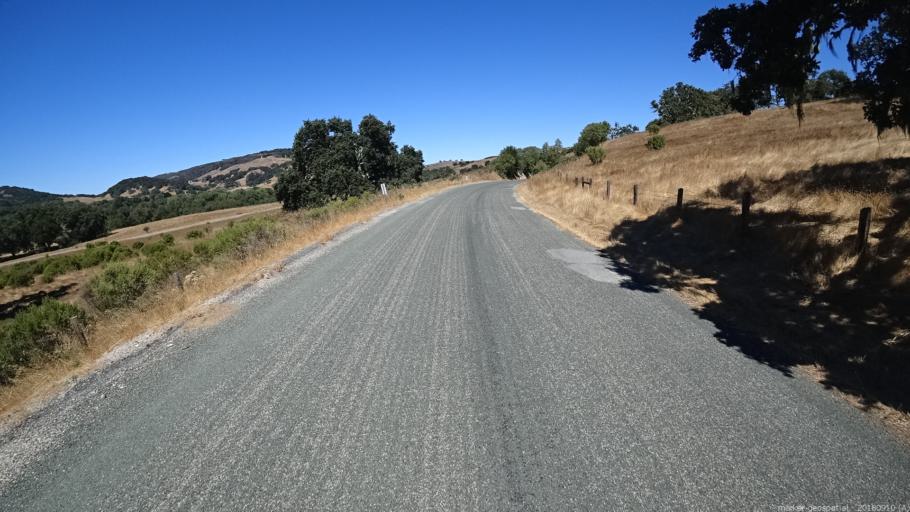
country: US
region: California
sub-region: Monterey County
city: Carmel Valley Village
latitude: 36.4526
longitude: -121.7974
